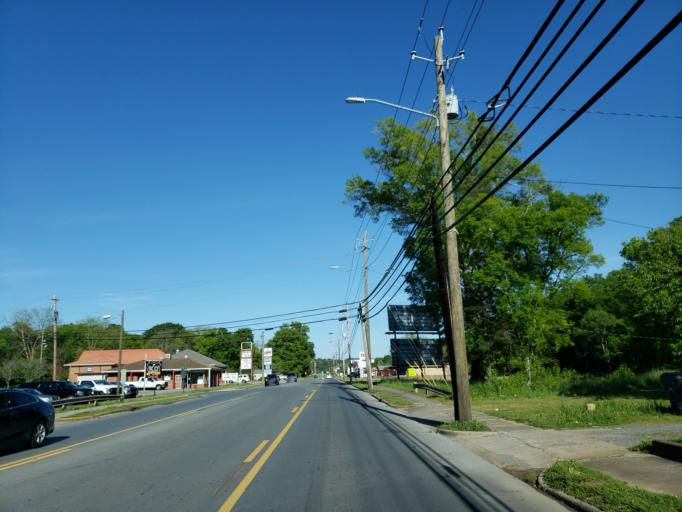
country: US
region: Georgia
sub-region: Polk County
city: Cedartown
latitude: 34.0143
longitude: -85.2429
